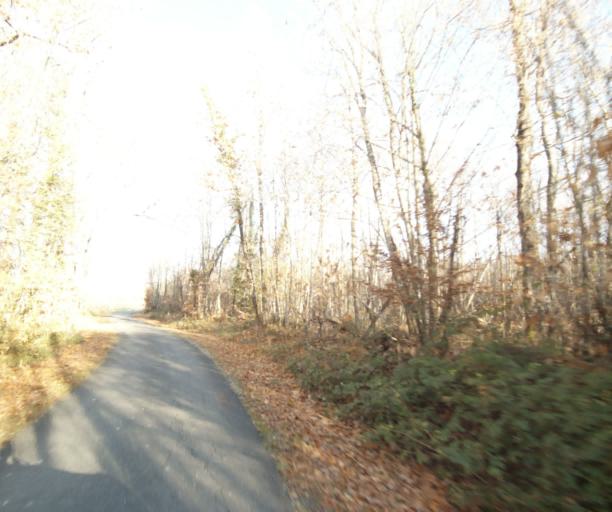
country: FR
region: Poitou-Charentes
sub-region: Departement de la Charente-Maritime
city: Cherac
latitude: 45.7335
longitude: -0.4654
